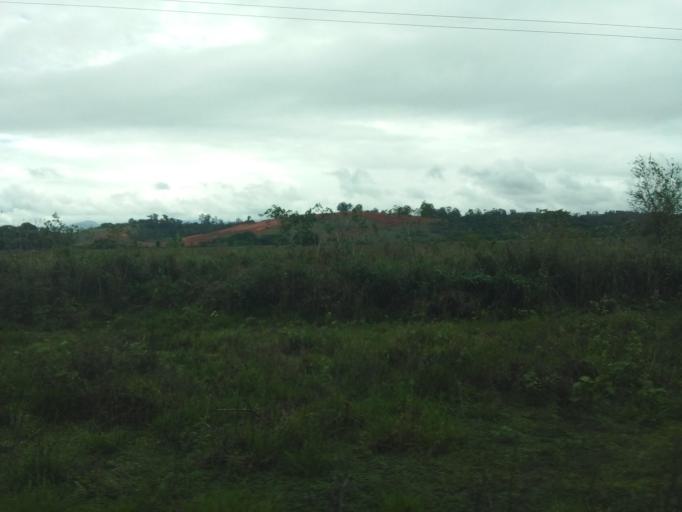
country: BR
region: Minas Gerais
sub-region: Ipatinga
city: Ipatinga
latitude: -19.4699
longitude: -42.4811
